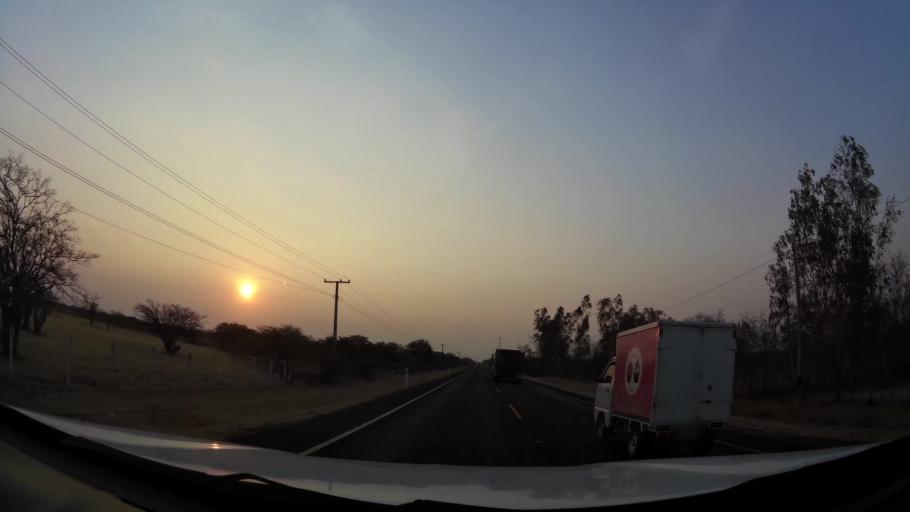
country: NI
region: Leon
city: La Paz Centro
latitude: 12.2917
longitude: -86.7629
